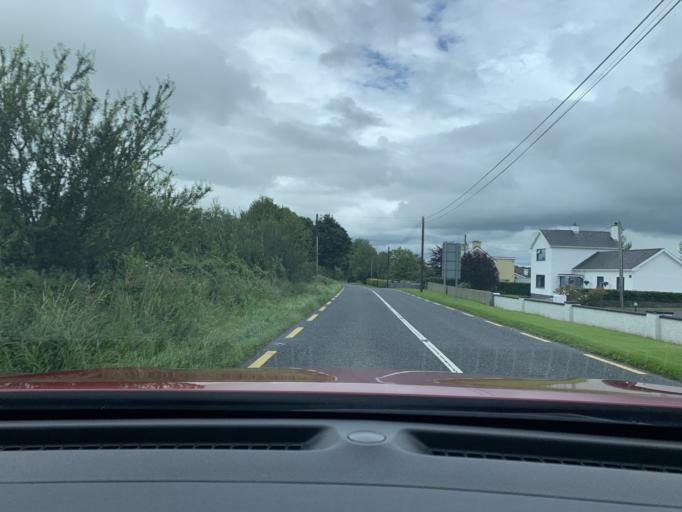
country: IE
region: Ulster
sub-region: County Donegal
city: Convoy
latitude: 54.7976
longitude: -7.6733
